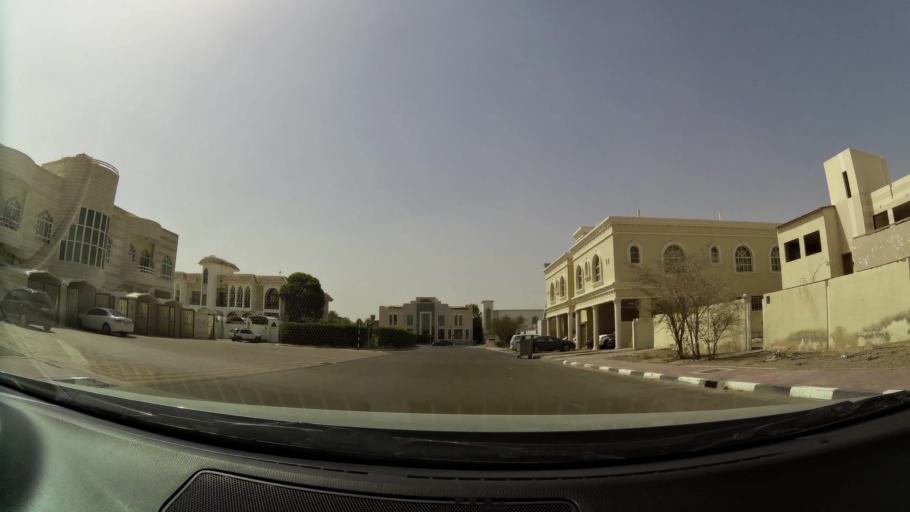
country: AE
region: Abu Dhabi
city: Al Ain
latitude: 24.2210
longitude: 55.6911
